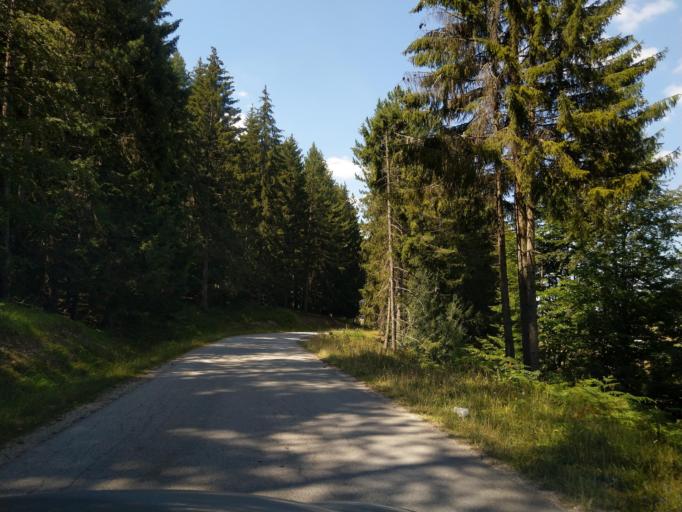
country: RS
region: Central Serbia
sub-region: Zlatiborski Okrug
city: Nova Varos
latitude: 43.4685
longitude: 19.9701
